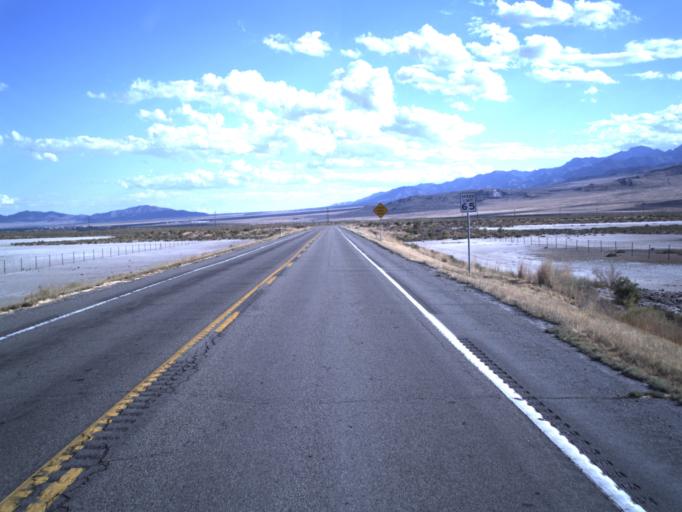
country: US
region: Utah
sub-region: Tooele County
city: Grantsville
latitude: 40.7034
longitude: -112.5300
